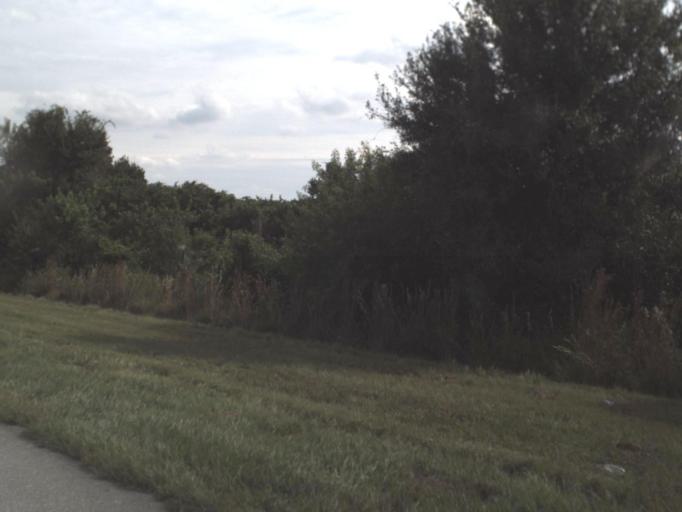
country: US
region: Florida
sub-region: Okeechobee County
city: Taylor Creek
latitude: 27.2077
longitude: -80.7511
